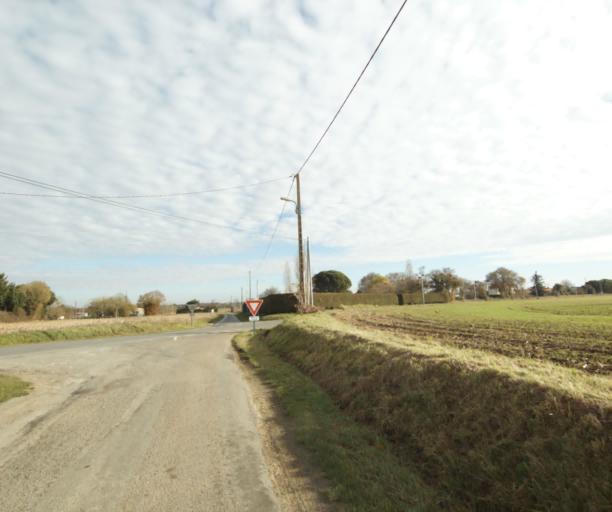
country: FR
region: Poitou-Charentes
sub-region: Departement de la Charente-Maritime
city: Corme-Royal
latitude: 45.7197
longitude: -0.8200
